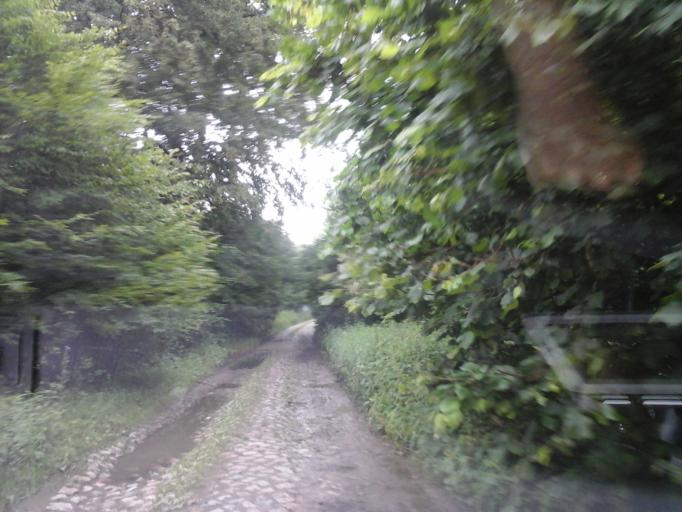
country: PL
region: West Pomeranian Voivodeship
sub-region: Powiat choszczenski
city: Krzecin
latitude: 53.0109
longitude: 15.4698
